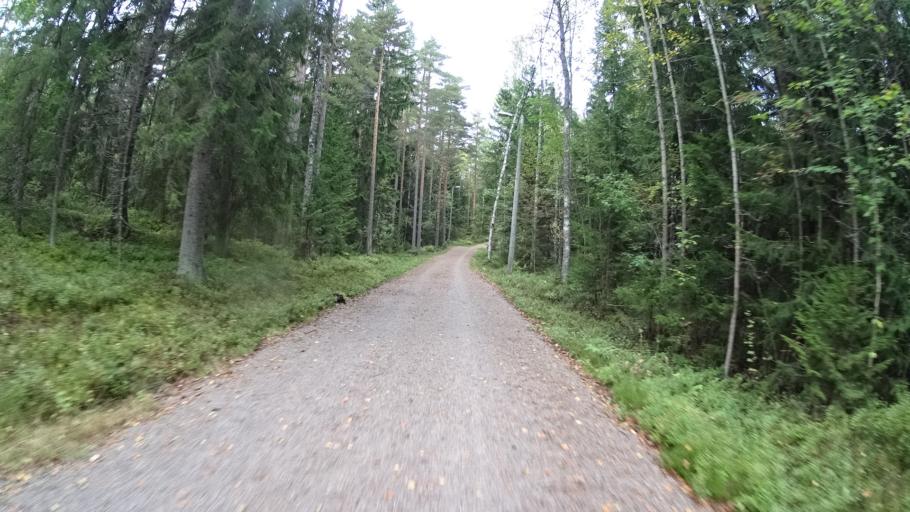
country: FI
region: Uusimaa
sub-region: Helsinki
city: Kauniainen
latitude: 60.1882
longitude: 24.7031
